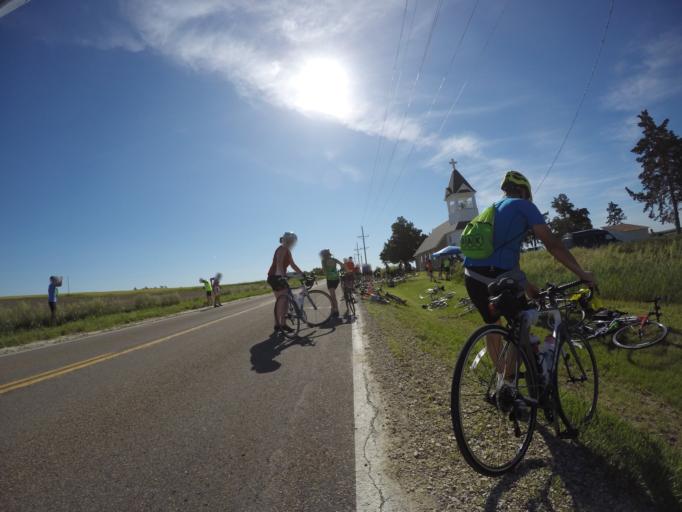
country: US
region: Kansas
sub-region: Mitchell County
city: Beloit
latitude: 39.6393
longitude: -97.9326
